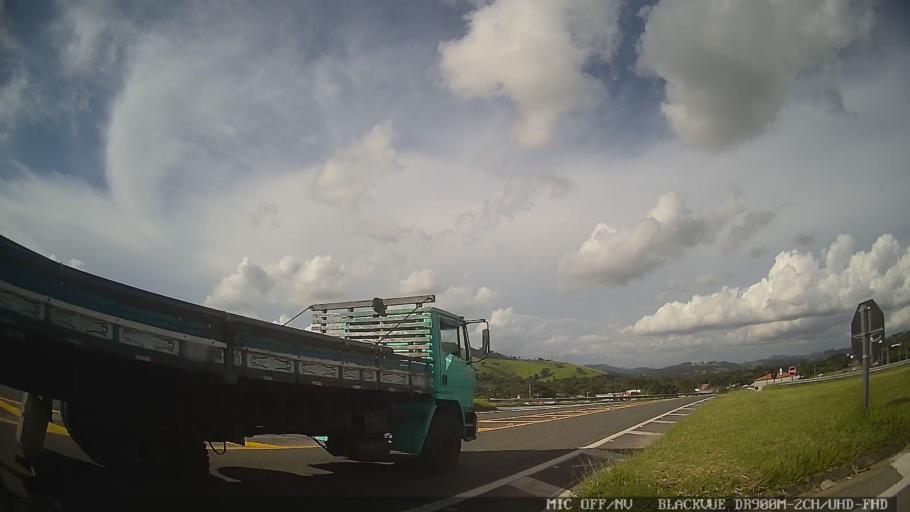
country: BR
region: Sao Paulo
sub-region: Bom Jesus Dos Perdoes
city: Bom Jesus dos Perdoes
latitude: -23.1145
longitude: -46.4832
